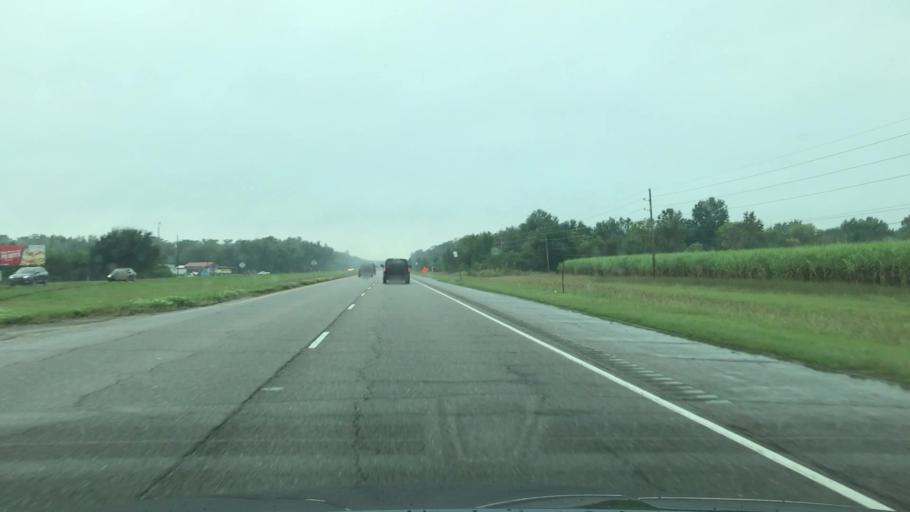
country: US
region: Louisiana
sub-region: Lafourche Parish
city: Raceland
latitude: 29.7394
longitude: -90.5575
